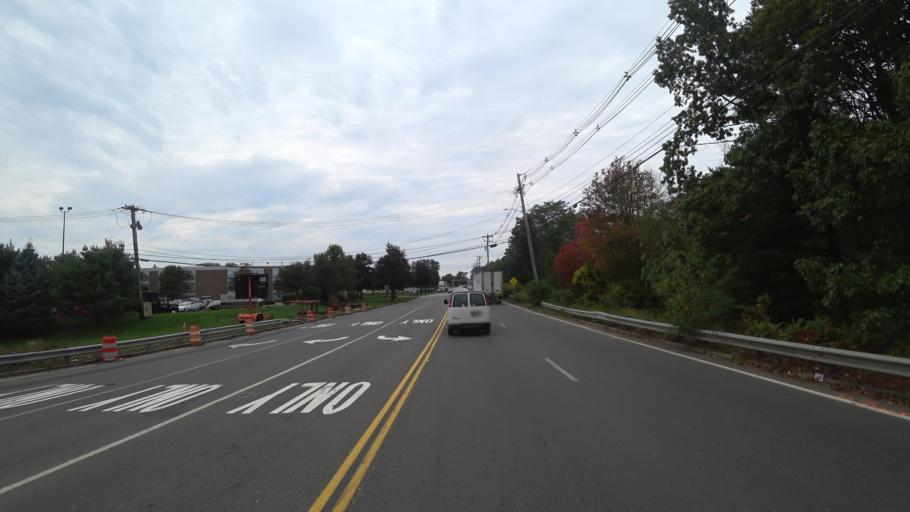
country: US
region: Massachusetts
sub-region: Middlesex County
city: Wilmington
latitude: 42.5876
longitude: -71.1557
